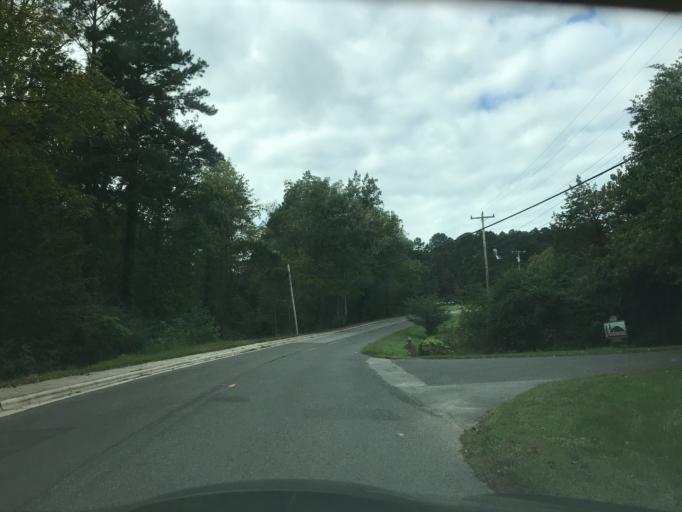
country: US
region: North Carolina
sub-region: Orange County
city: Chapel Hill
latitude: 35.9227
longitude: -79.0664
